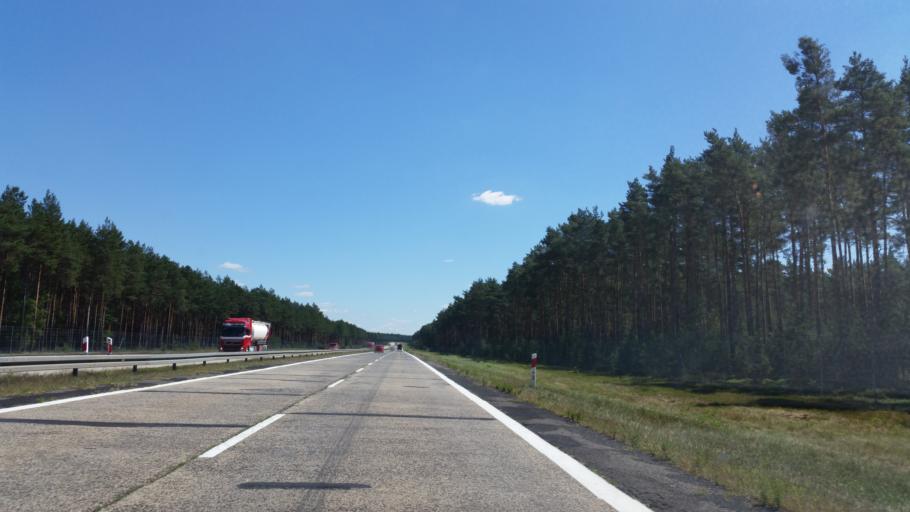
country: PL
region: Lubusz
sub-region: Powiat zaganski
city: Malomice
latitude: 51.4234
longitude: 15.4511
